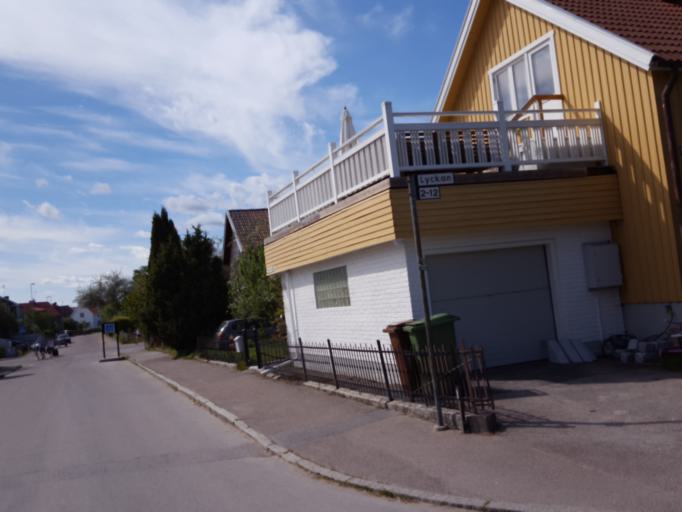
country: SE
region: Uppsala
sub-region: Uppsala Kommun
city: Uppsala
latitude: 59.8589
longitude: 17.6659
